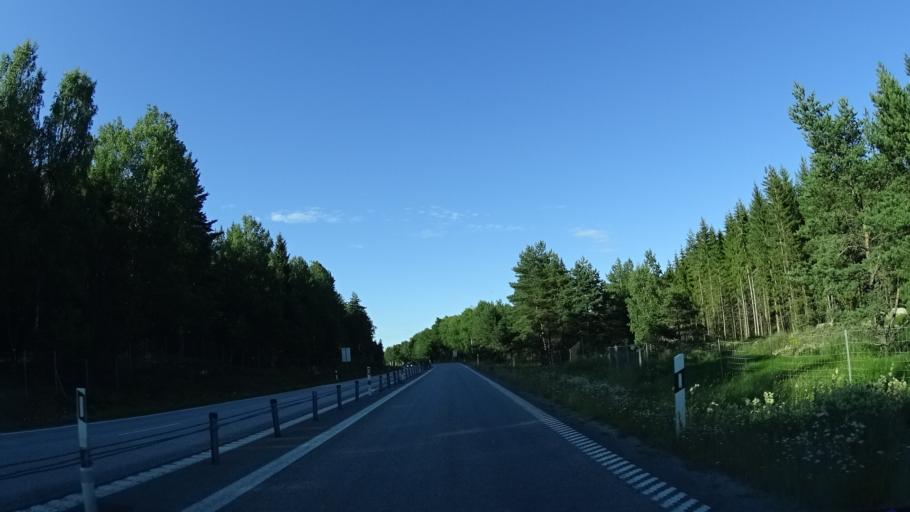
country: SE
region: Stockholm
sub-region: Vallentuna Kommun
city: Vallentuna
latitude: 59.5239
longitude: 18.1862
